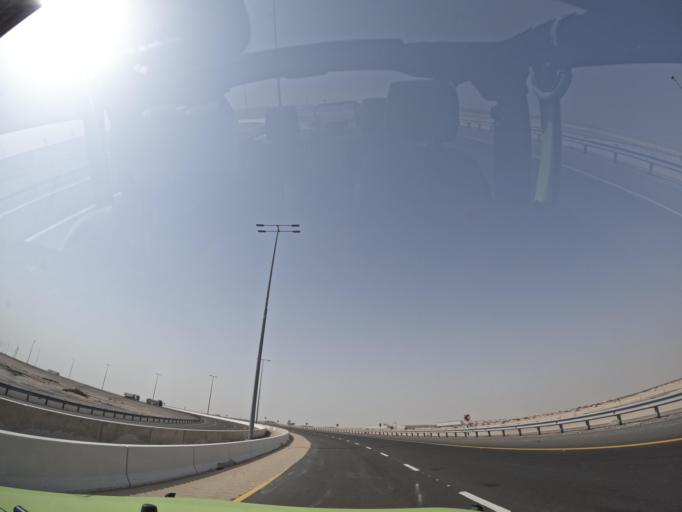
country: AE
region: Dubai
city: Dubai
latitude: 24.7910
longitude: 55.0756
